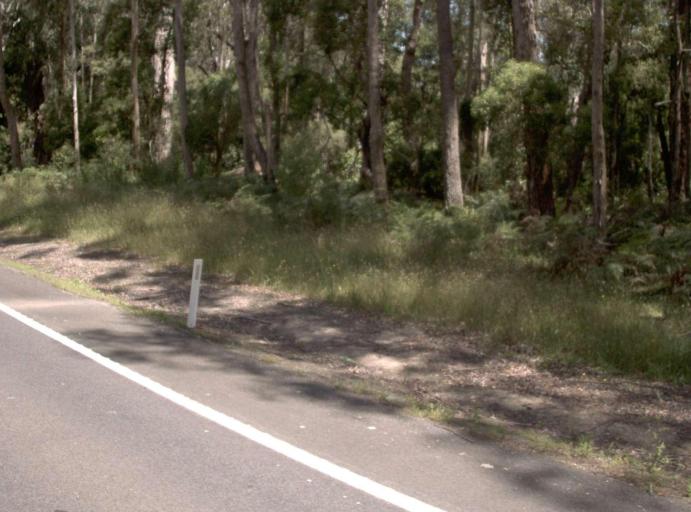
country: AU
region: New South Wales
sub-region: Bombala
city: Bombala
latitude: -37.5634
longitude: 149.0711
